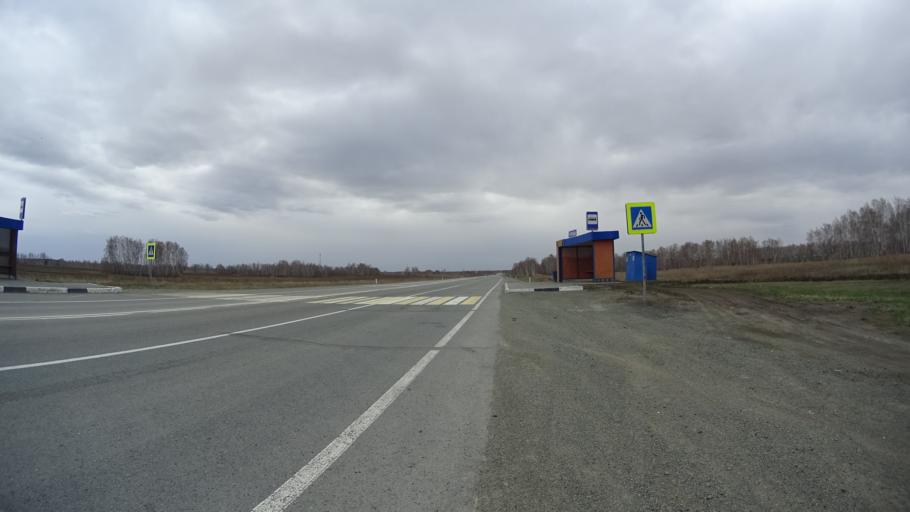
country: RU
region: Chelyabinsk
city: Yemanzhelinsk
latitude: 54.6965
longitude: 61.2499
